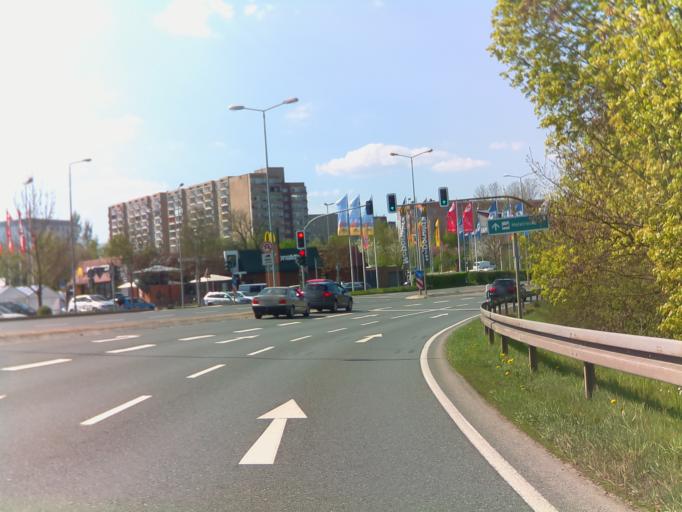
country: DE
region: Saxony
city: Plauen
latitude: 50.4963
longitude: 12.1728
